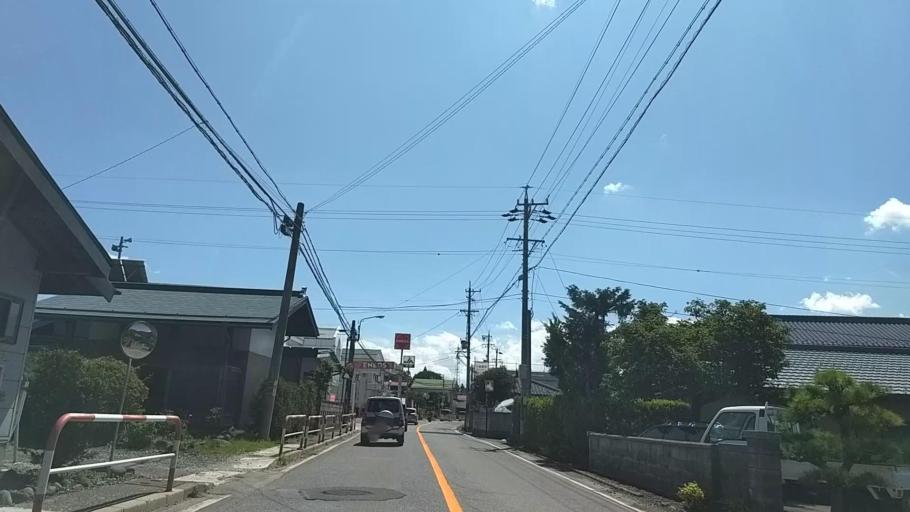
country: JP
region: Nagano
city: Chino
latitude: 36.0417
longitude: 138.2252
